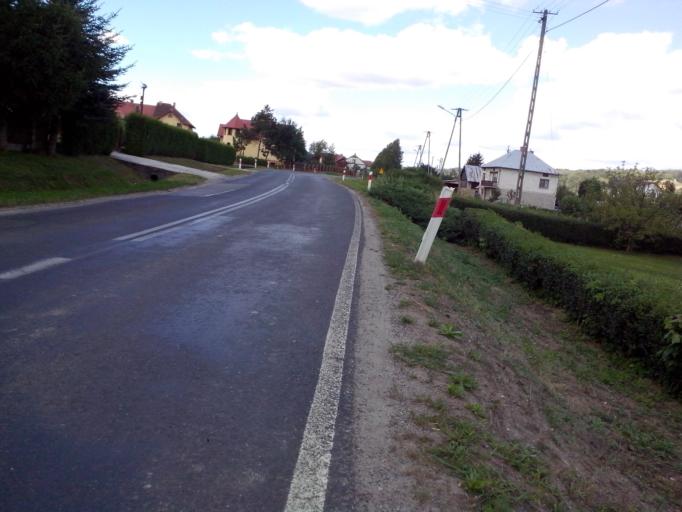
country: PL
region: Subcarpathian Voivodeship
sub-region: Powiat strzyzowski
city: Strzyzow
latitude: 49.8349
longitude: 21.8257
